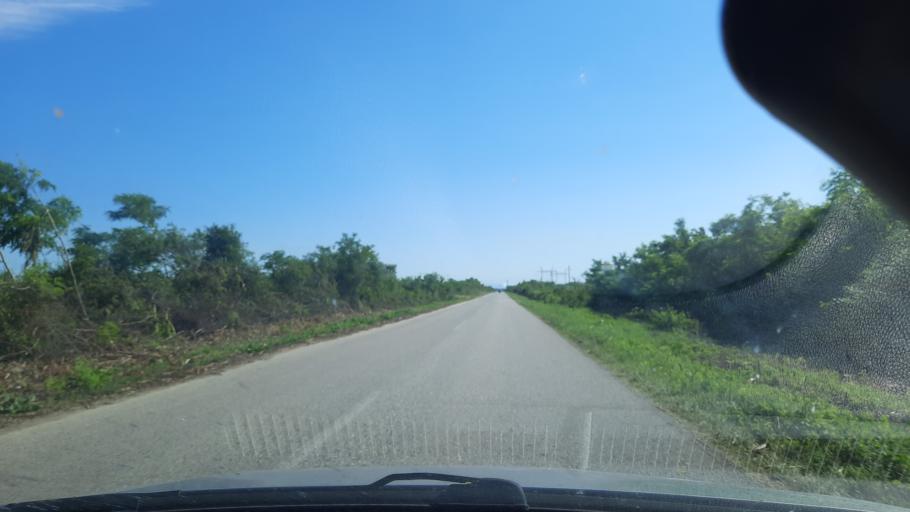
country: RS
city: Simanovci
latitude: 44.7939
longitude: 20.0926
